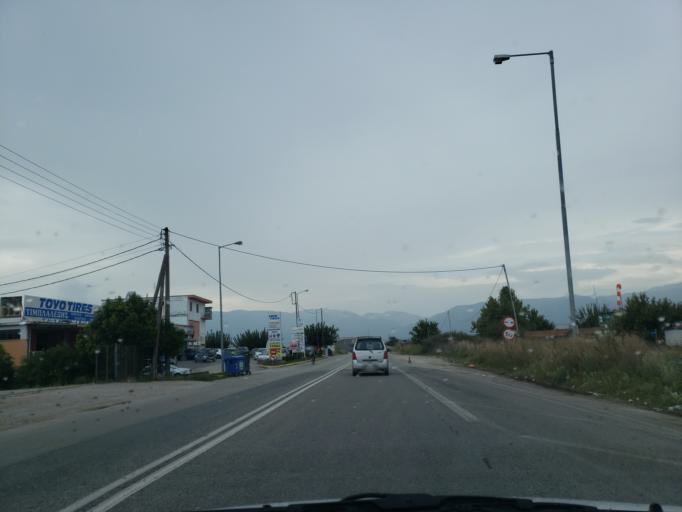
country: GR
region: Central Greece
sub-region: Nomos Fthiotidos
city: Lamia
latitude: 38.8730
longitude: 22.4394
